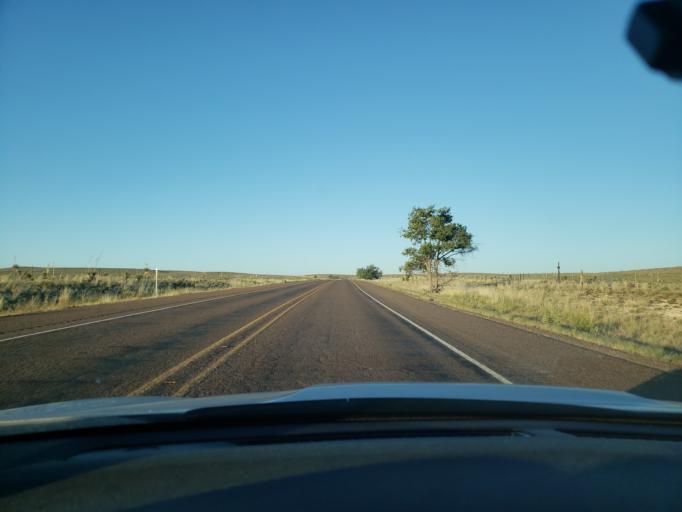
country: US
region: Texas
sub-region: El Paso County
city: Homestead Meadows South
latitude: 31.8329
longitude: -105.8596
